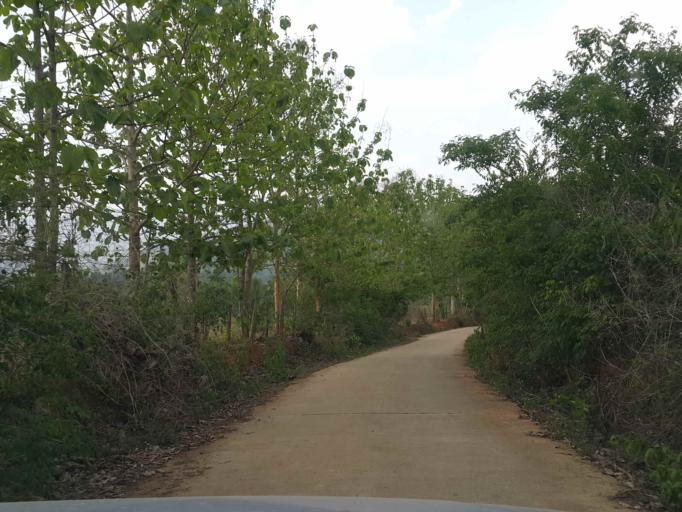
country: TH
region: Chiang Mai
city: Wiang Haeng
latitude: 19.3736
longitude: 98.7200
